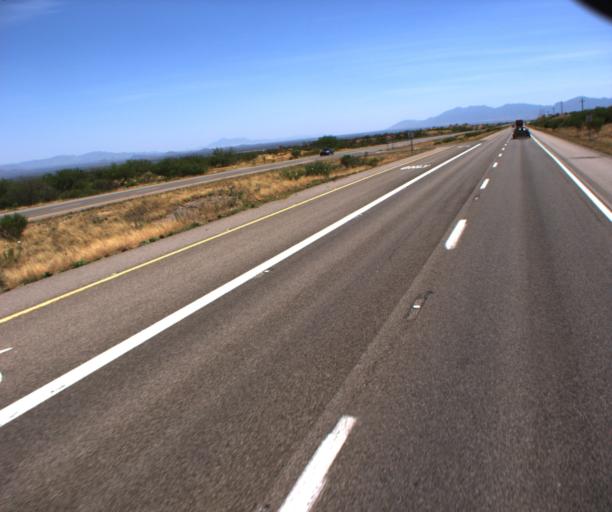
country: US
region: Arizona
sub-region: Cochise County
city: Whetstone
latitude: 31.8598
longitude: -110.3413
